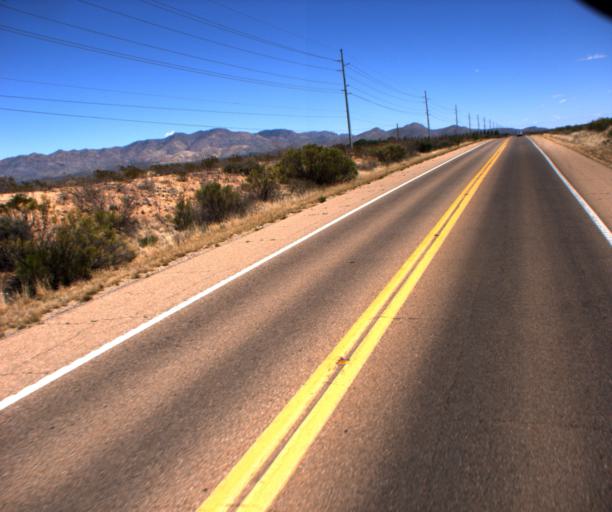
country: US
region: Arizona
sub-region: Cochise County
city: Sierra Vista Southeast
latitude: 31.3800
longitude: -110.0946
